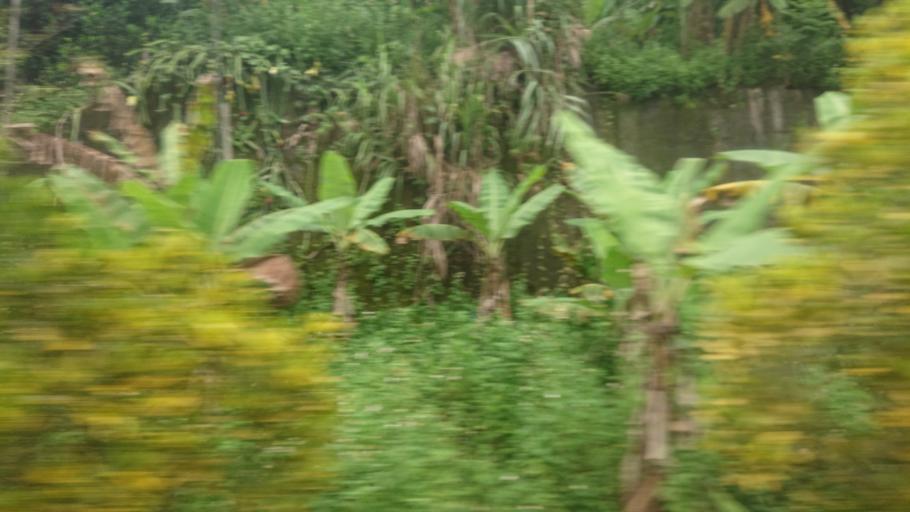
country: TW
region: Taiwan
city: Lugu
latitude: 23.8241
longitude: 120.8307
